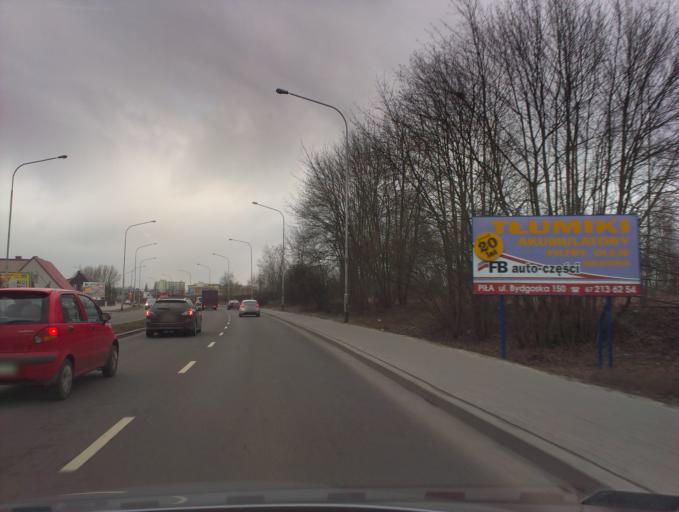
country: PL
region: Greater Poland Voivodeship
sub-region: Powiat pilski
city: Pila
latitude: 53.1405
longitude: 16.7496
